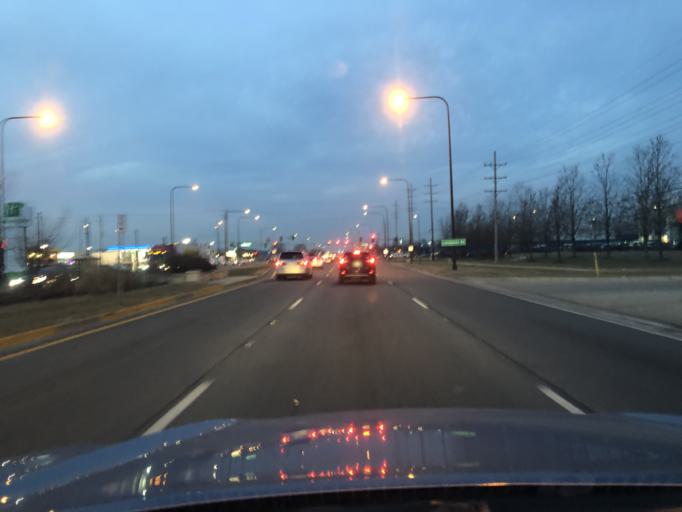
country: US
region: Illinois
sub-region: Cook County
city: Elk Grove Village
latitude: 42.0098
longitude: -87.9597
